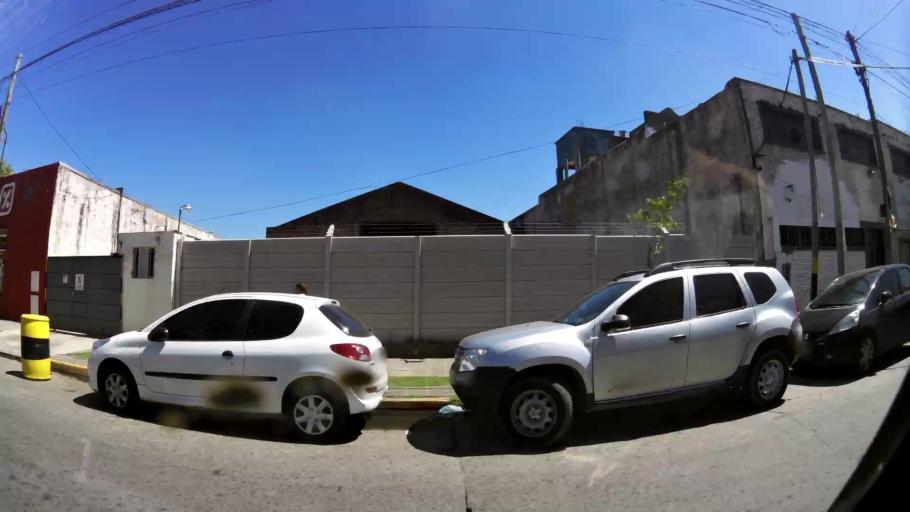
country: AR
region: Buenos Aires
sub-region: Partido de Quilmes
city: Quilmes
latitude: -34.7158
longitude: -58.2729
